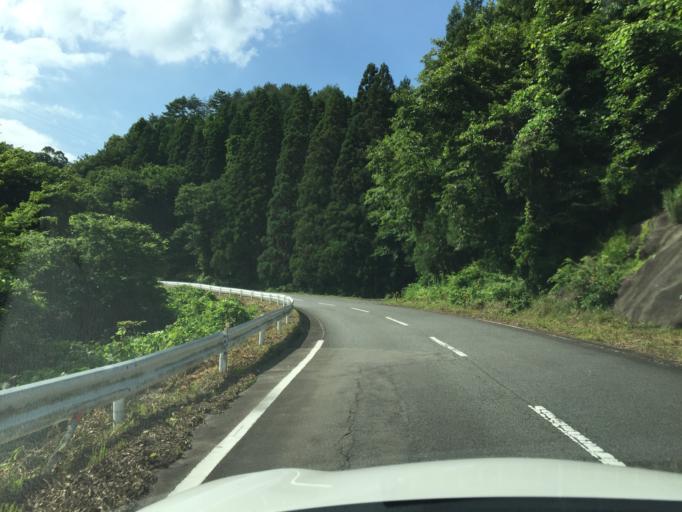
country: JP
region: Fukushima
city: Ishikawa
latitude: 37.1255
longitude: 140.6433
